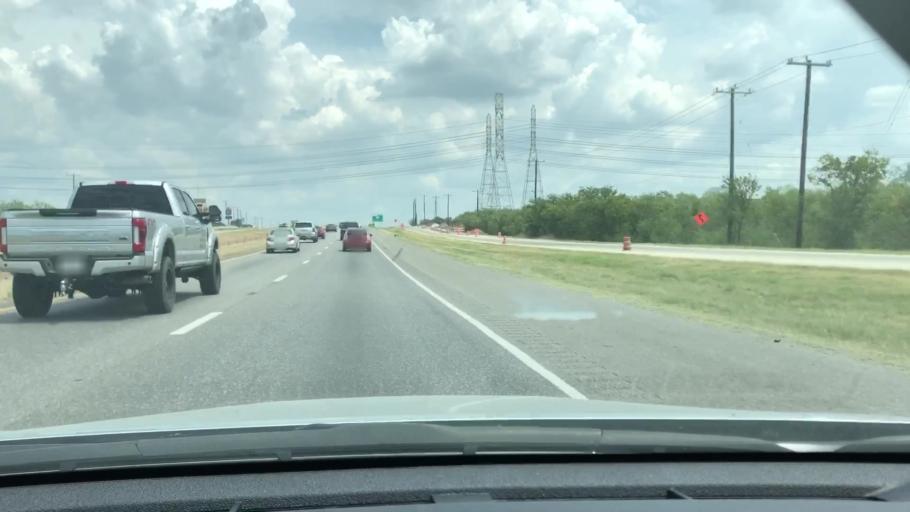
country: US
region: Texas
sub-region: Bexar County
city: Kirby
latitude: 29.4551
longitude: -98.3260
